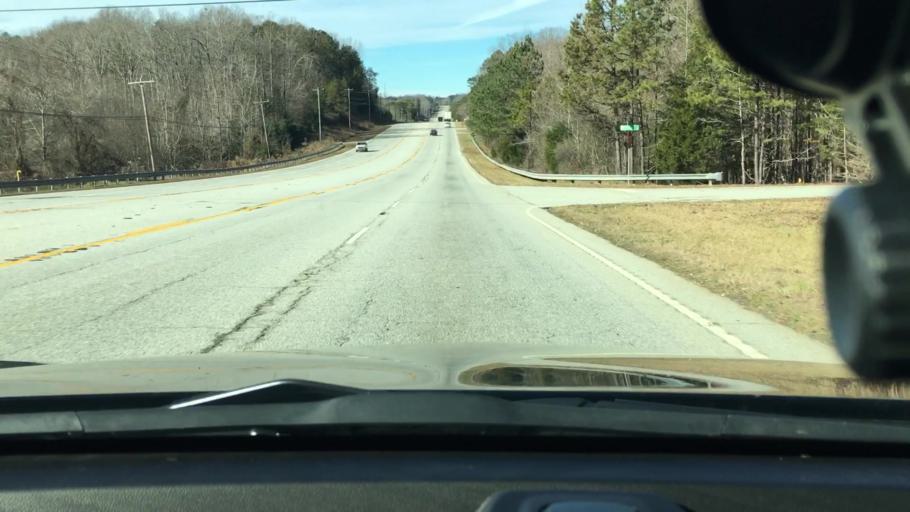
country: US
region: South Carolina
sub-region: Spartanburg County
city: Pacolet
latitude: 34.9114
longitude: -81.8053
